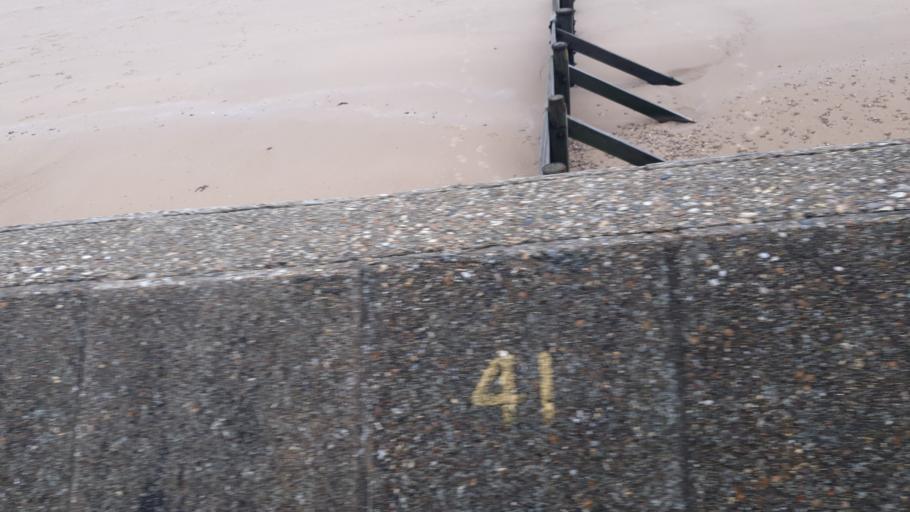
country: GB
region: England
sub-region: Essex
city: Frinton-on-Sea
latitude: 51.8347
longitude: 1.2555
